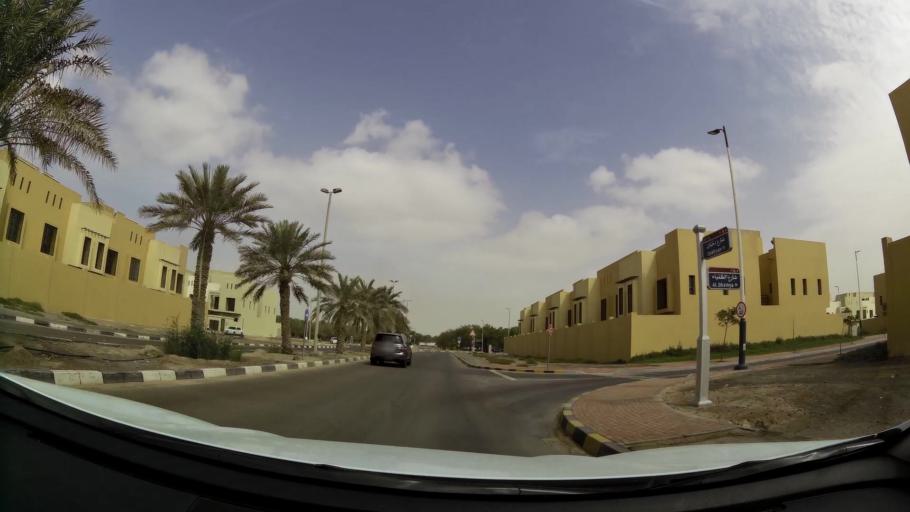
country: AE
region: Abu Dhabi
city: Abu Dhabi
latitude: 24.3980
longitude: 54.4938
